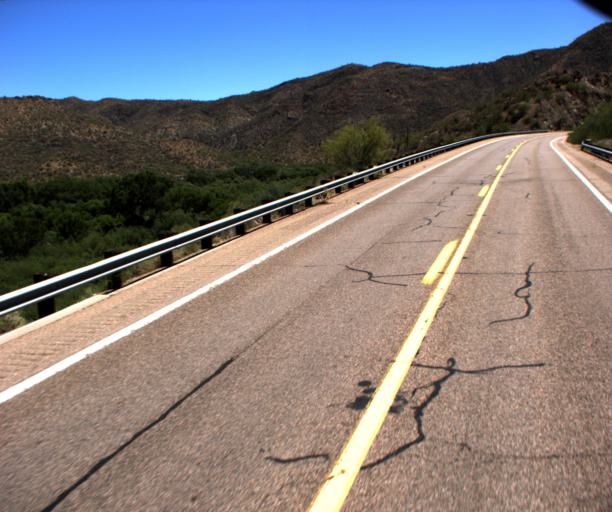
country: US
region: Arizona
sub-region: Pinal County
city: Kearny
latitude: 33.0481
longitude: -110.7176
